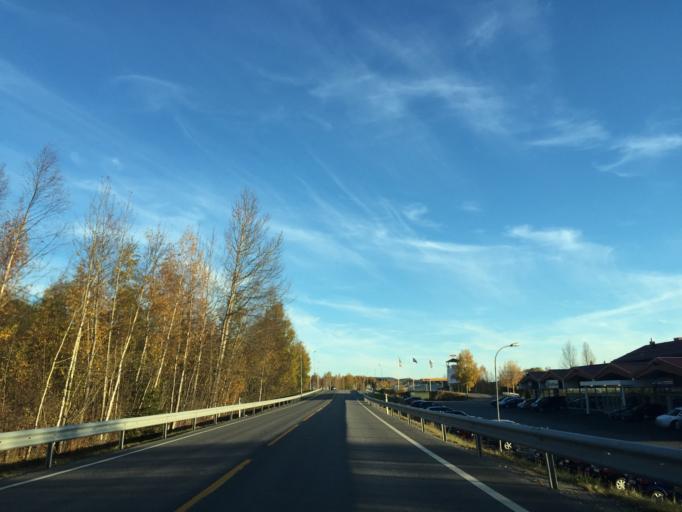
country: NO
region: Hedmark
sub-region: Kongsvinger
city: Kongsvinger
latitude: 60.2100
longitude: 11.9635
